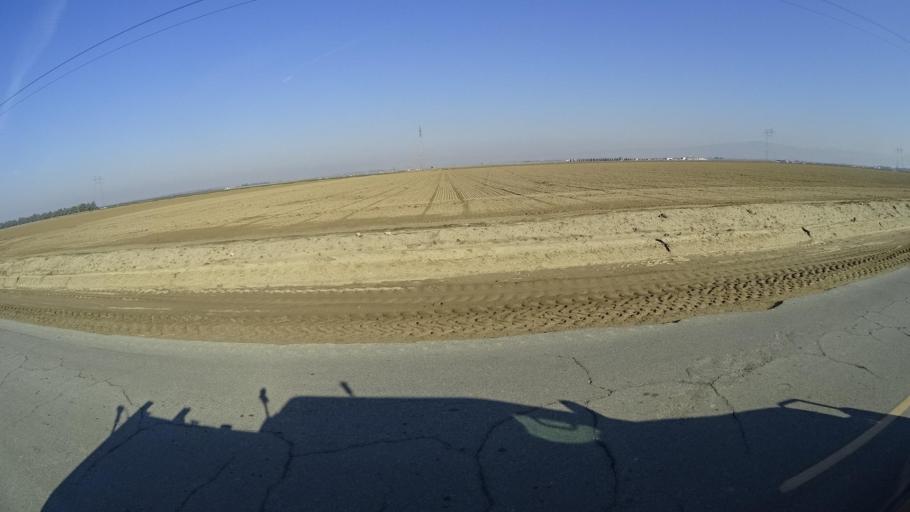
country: US
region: California
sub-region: Kern County
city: Weedpatch
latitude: 35.1221
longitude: -118.9496
